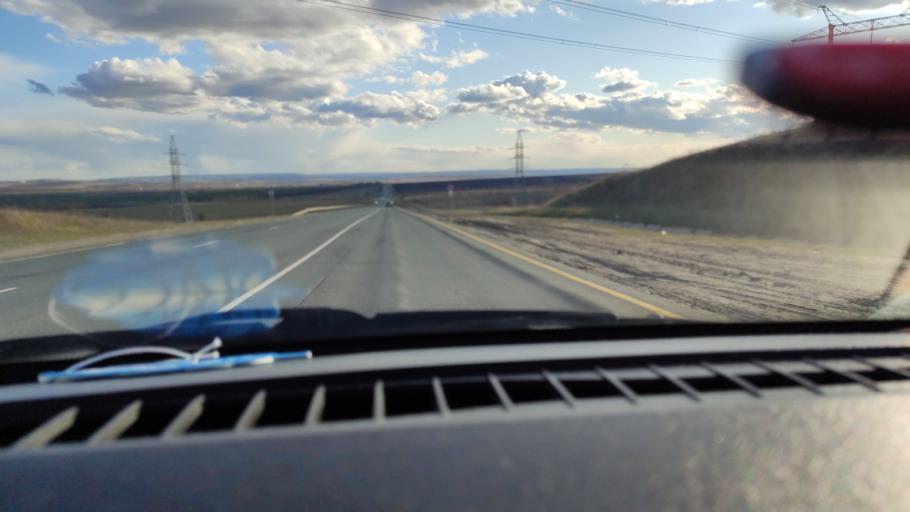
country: RU
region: Saratov
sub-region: Saratovskiy Rayon
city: Saratov
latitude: 51.7617
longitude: 46.0726
